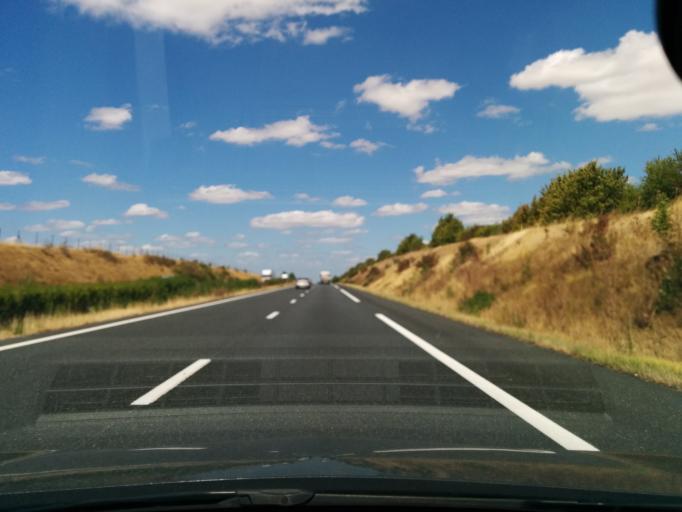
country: FR
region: Centre
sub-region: Departement de l'Indre
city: Vatan
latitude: 47.0264
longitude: 1.7889
